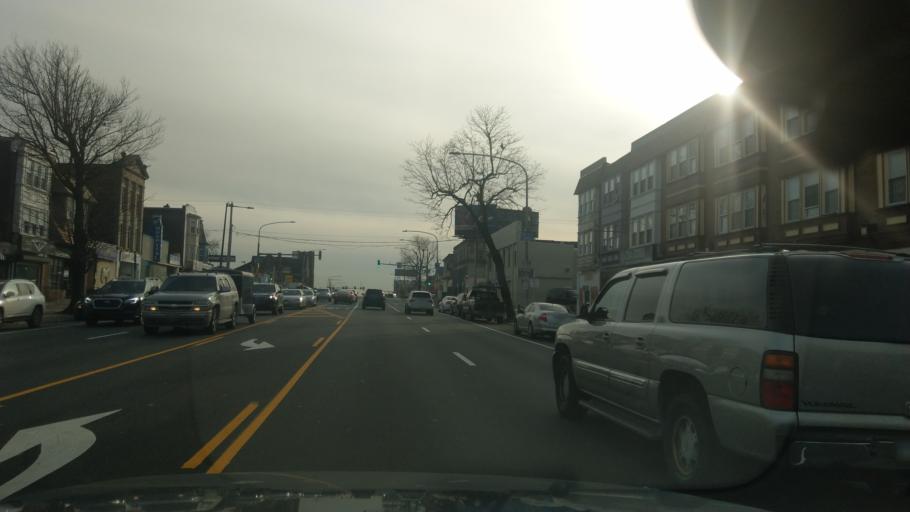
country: US
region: Pennsylvania
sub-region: Montgomery County
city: Wyncote
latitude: 40.0439
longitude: -75.1437
